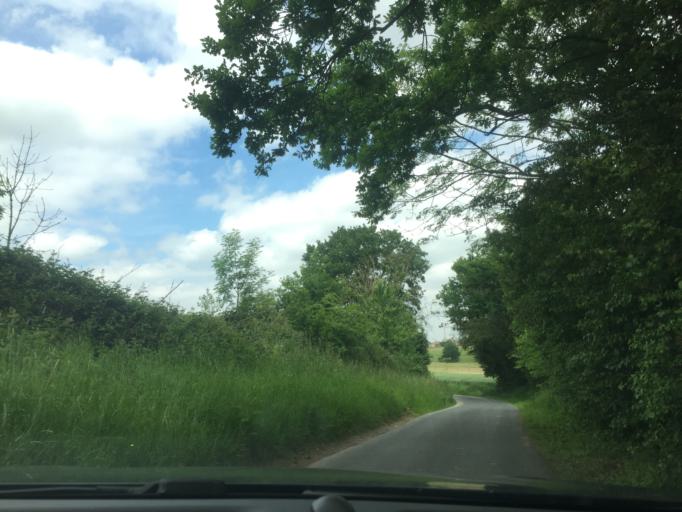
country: BE
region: Flanders
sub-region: Provincie West-Vlaanderen
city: Zwevegem
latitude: 50.7731
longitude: 3.3330
